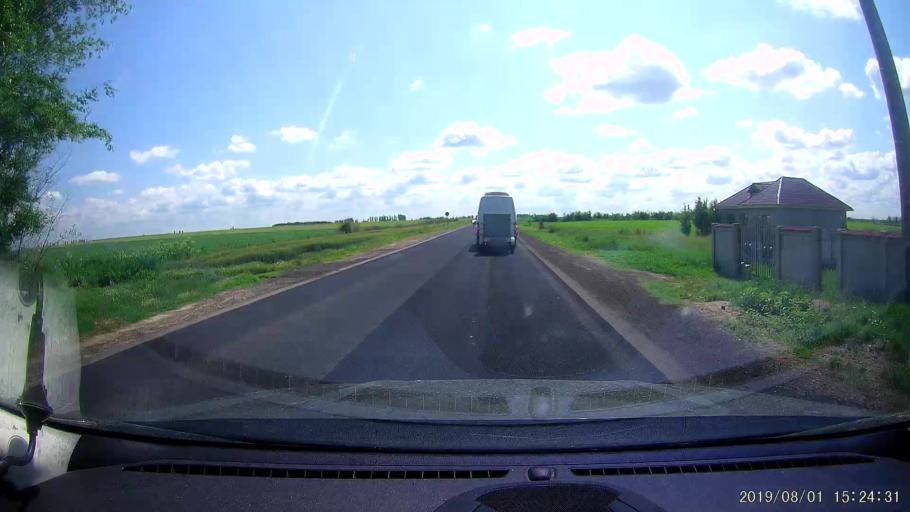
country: RO
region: Braila
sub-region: Comuna Viziru
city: Lanurile
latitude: 45.0323
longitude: 27.7485
